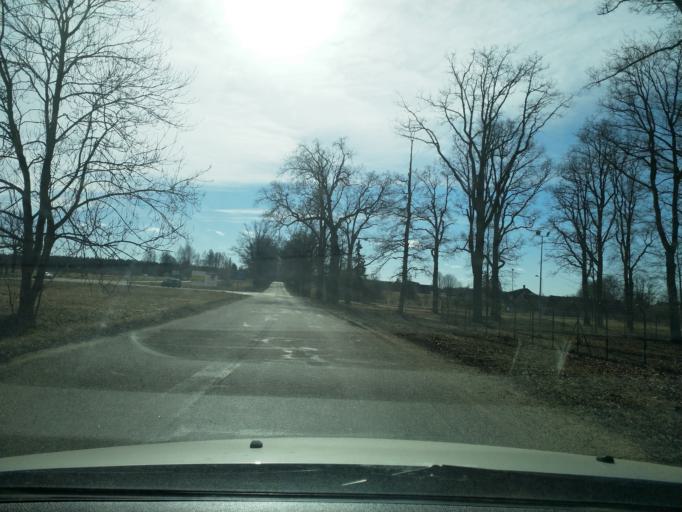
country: LV
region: Valmieras Rajons
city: Valmiera
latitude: 57.5193
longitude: 25.4196
